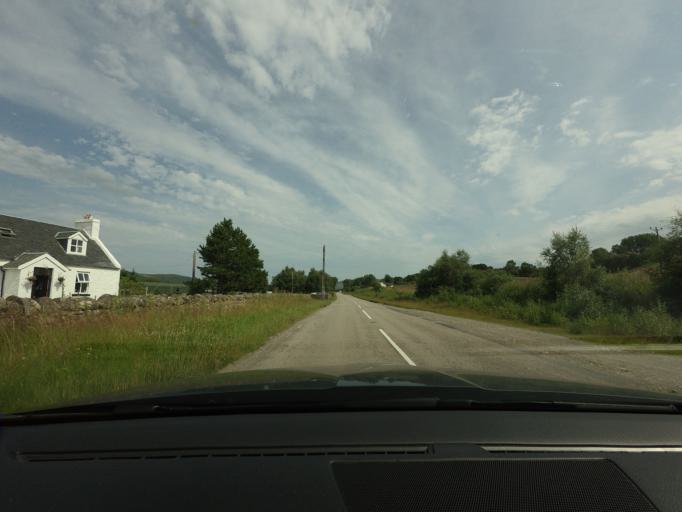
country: GB
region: Scotland
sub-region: Highland
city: Alness
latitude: 57.8715
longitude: -4.3496
